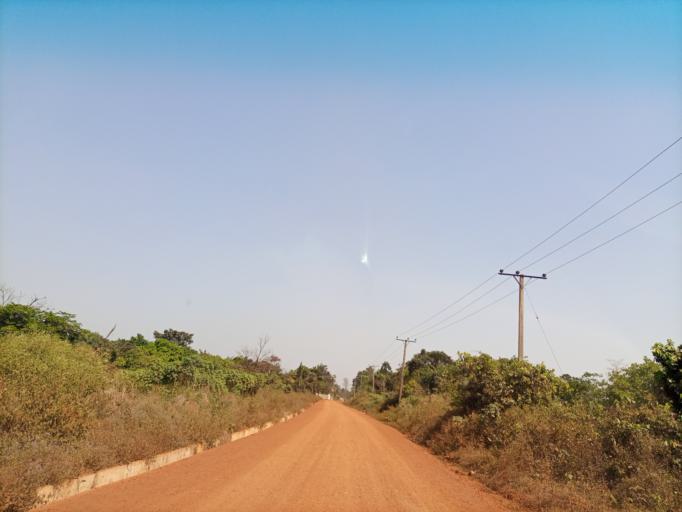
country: NG
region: Enugu
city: Nsukka
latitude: 6.7993
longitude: 7.3481
